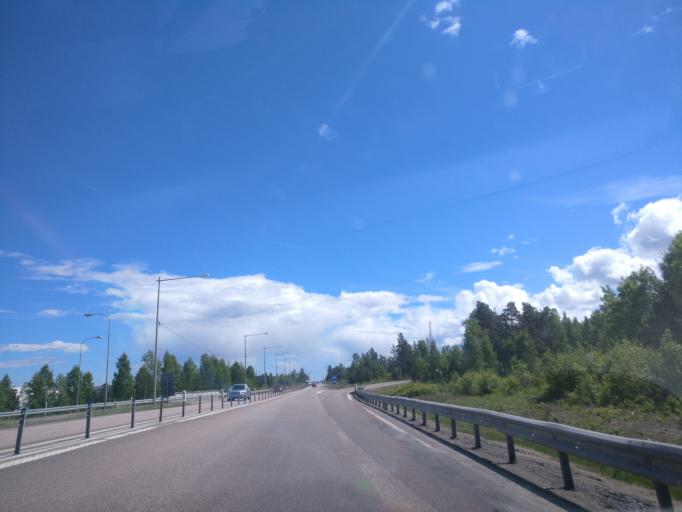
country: SE
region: Vaesternorrland
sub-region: Haernoesands Kommun
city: Haernoesand
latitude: 62.6540
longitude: 17.8825
